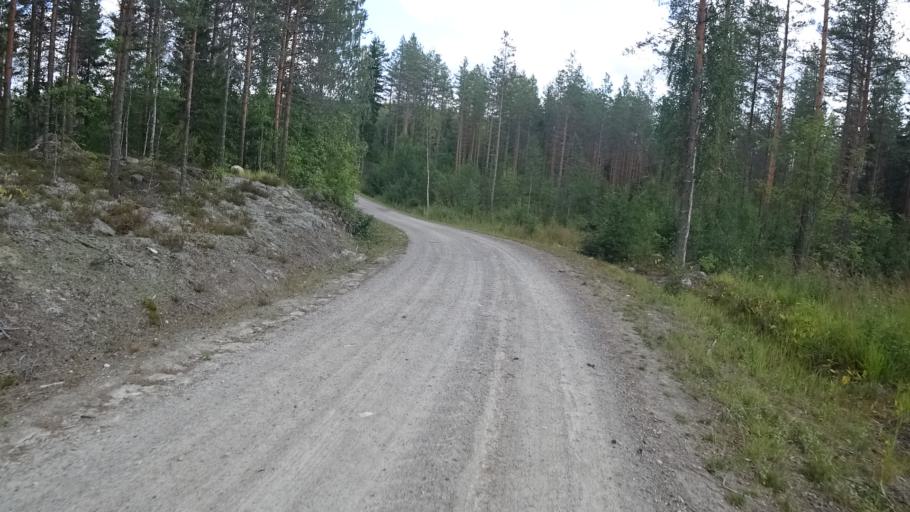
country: FI
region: North Karelia
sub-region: Joensuu
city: Ilomantsi
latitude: 62.6187
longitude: 31.2312
